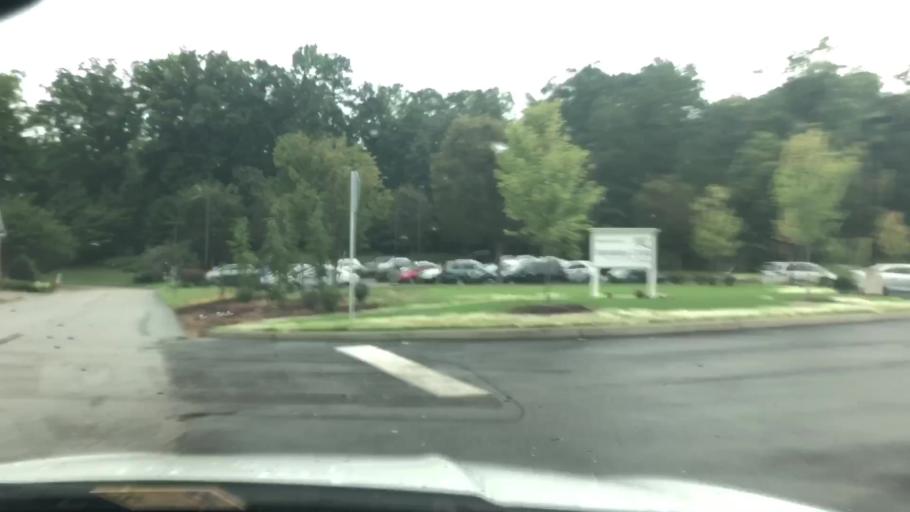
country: US
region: Virginia
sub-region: James City County
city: Williamsburg
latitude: 37.2403
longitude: -76.7655
